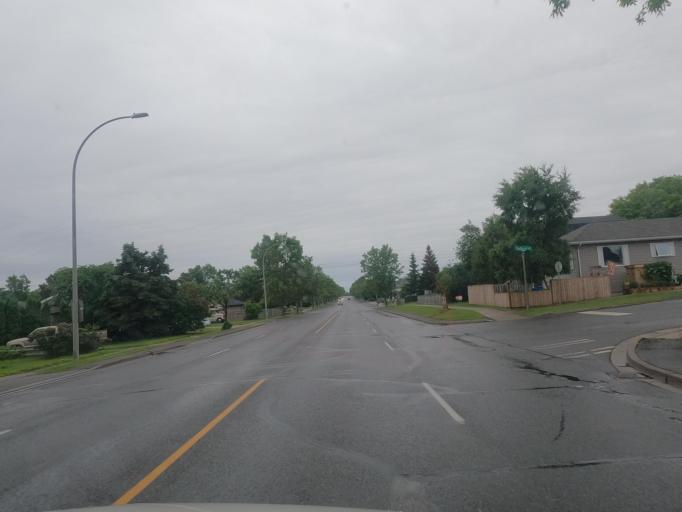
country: CA
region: Ontario
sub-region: Thunder Bay District
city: Thunder Bay
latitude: 48.4654
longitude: -89.1823
